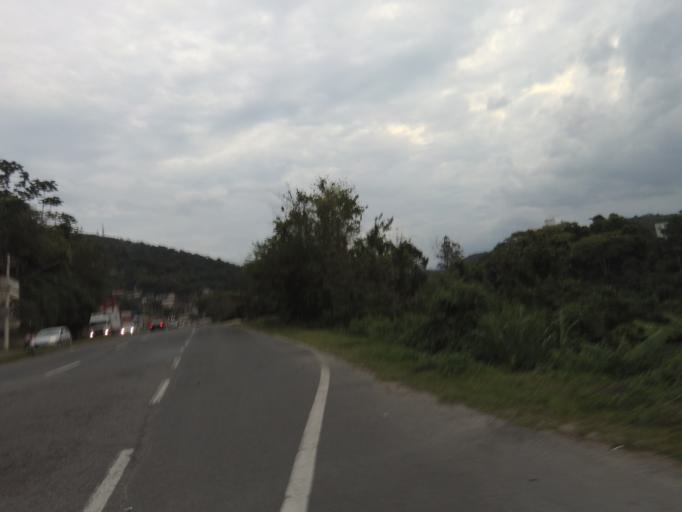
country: BR
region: Santa Catarina
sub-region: Blumenau
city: Blumenau
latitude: -26.8955
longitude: -49.0584
